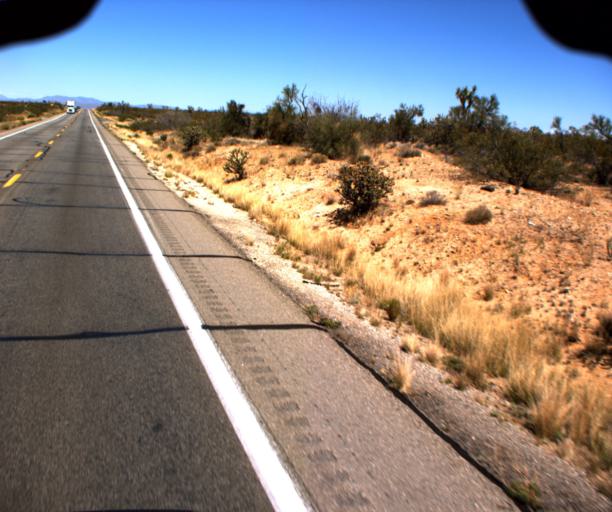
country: US
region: Arizona
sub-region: Yavapai County
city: Congress
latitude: 34.2423
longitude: -113.0771
